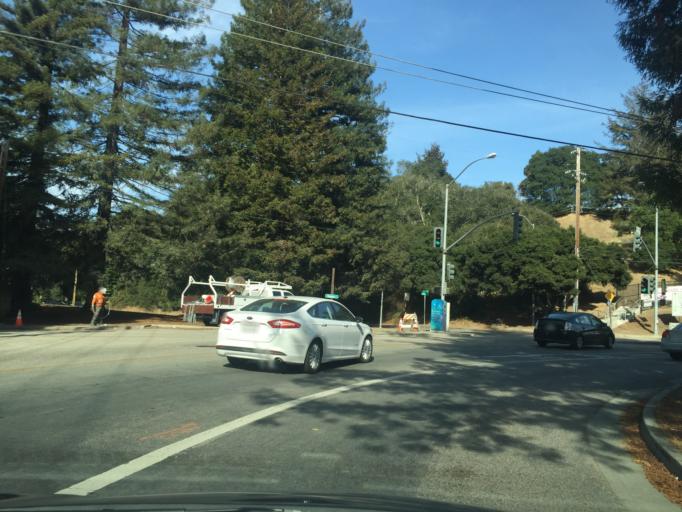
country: US
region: California
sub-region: Santa Cruz County
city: Aptos
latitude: 36.9763
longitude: -121.8856
